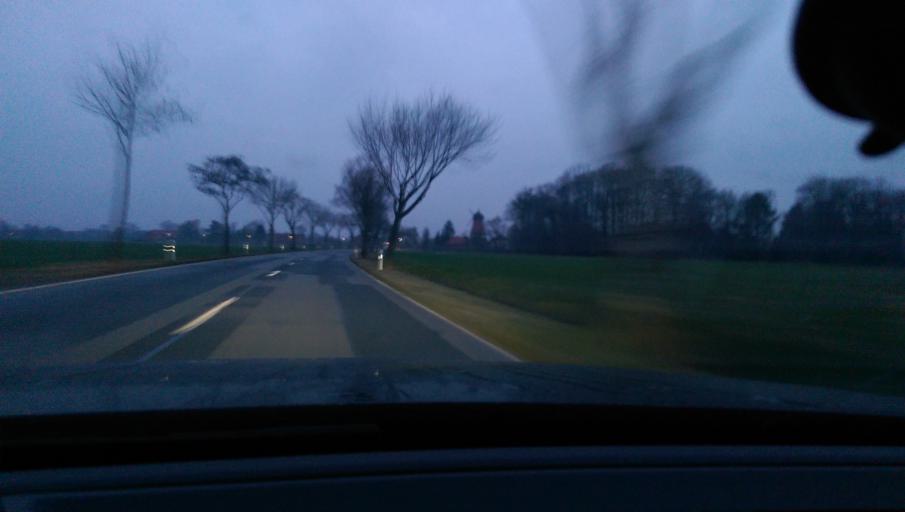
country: DE
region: Lower Saxony
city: Grossgoltern
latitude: 52.3516
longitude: 9.5478
